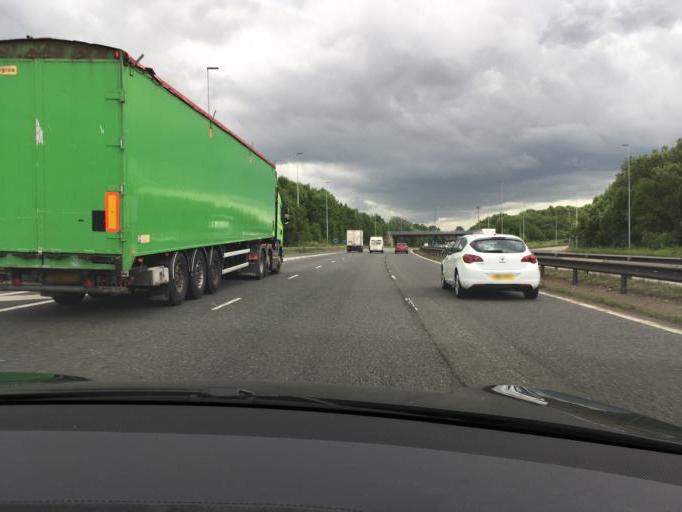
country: GB
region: England
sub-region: Borough of Stockport
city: Cheadle Heath
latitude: 53.4016
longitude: -2.2120
